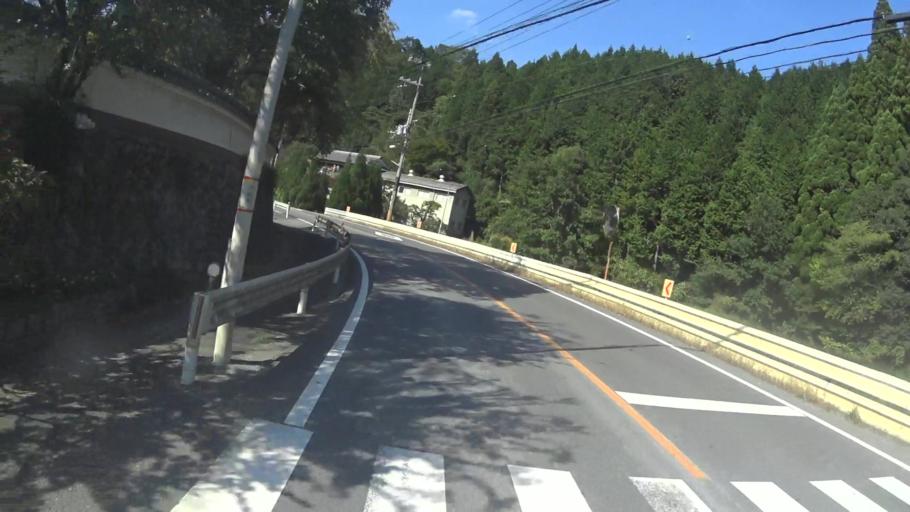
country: JP
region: Kyoto
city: Kameoka
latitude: 34.9441
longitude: 135.5522
